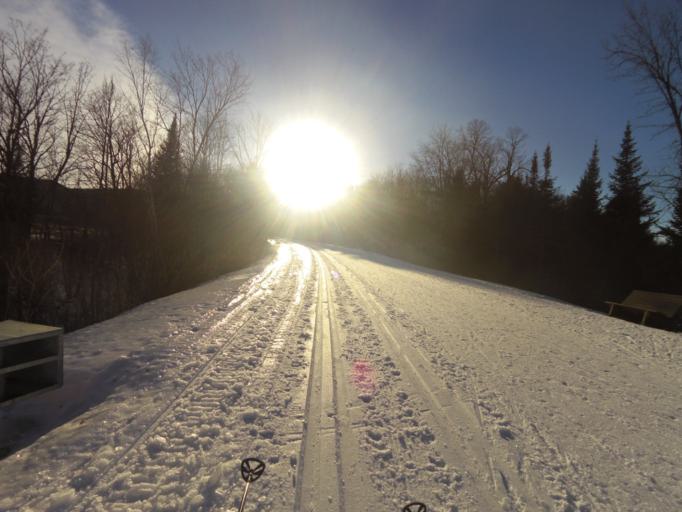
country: CA
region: Quebec
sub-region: Outaouais
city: Wakefield
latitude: 45.5253
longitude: -75.8411
